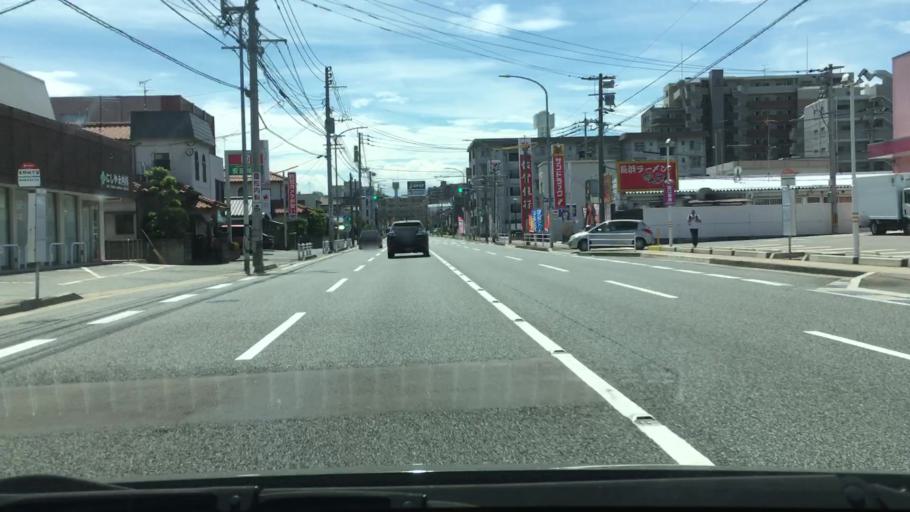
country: JP
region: Fukuoka
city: Onojo
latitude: 33.5515
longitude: 130.4575
